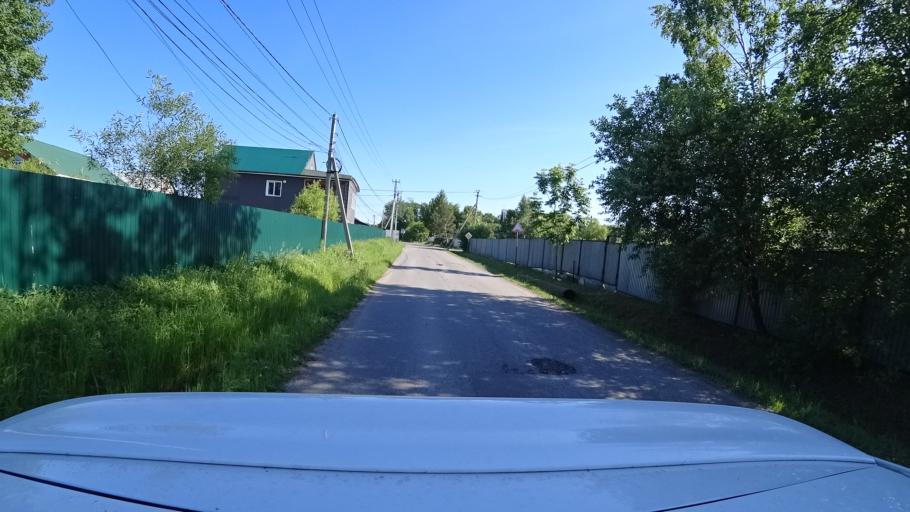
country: RU
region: Khabarovsk Krai
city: Topolevo
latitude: 48.5441
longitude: 135.1739
